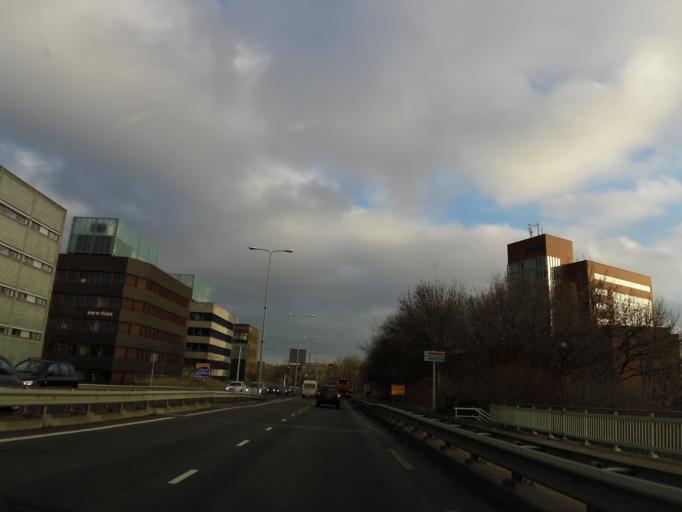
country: NL
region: Limburg
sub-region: Gemeente Maastricht
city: Maastricht
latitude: 50.8410
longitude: 5.7028
